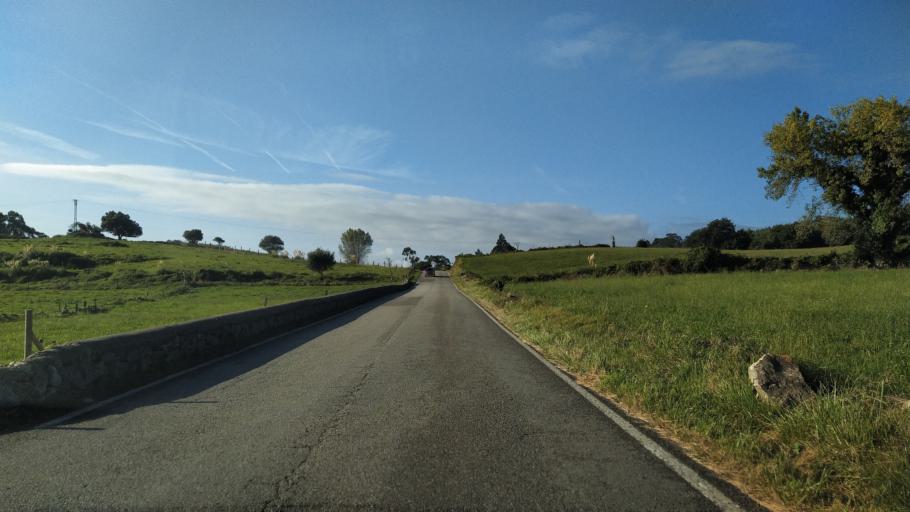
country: ES
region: Cantabria
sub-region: Provincia de Cantabria
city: Santa Cruz de Bezana
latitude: 43.4541
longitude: -3.9280
